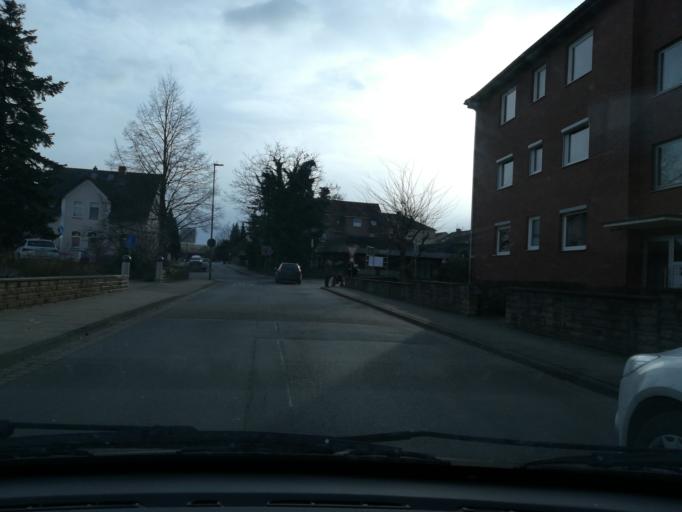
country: DE
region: Lower Saxony
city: Garbsen
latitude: 52.4010
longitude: 9.5591
